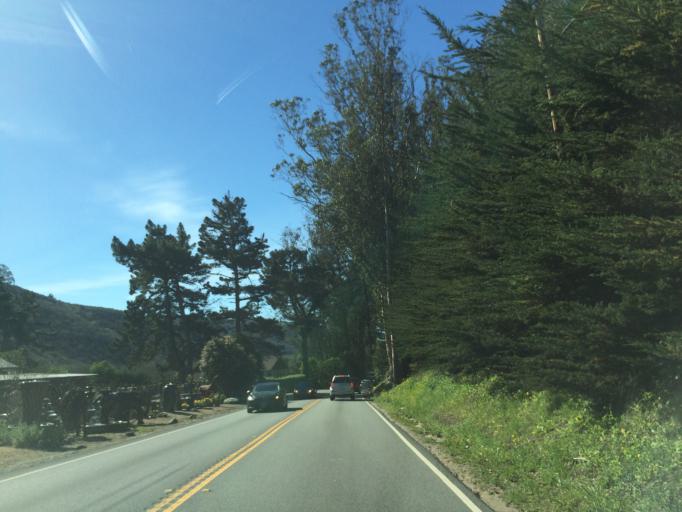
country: US
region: California
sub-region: San Mateo County
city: Half Moon Bay
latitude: 37.4851
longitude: -122.3988
